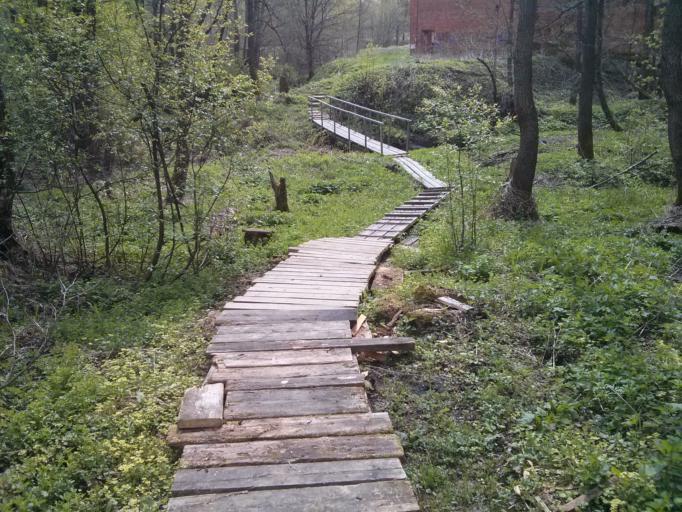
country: RU
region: Nizjnij Novgorod
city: Shimorskoye
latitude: 55.3092
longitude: 41.8523
